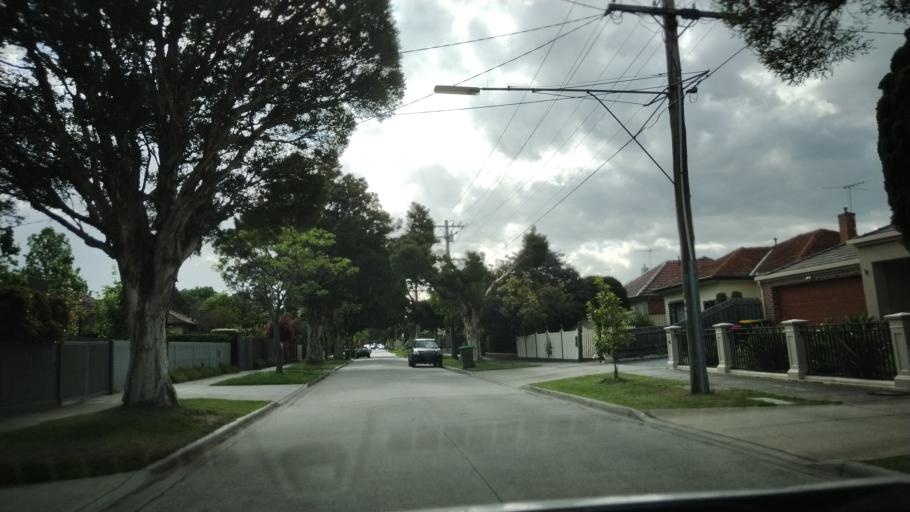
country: AU
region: Victoria
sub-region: Glen Eira
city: Glen Huntly
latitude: -37.8971
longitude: 145.0522
